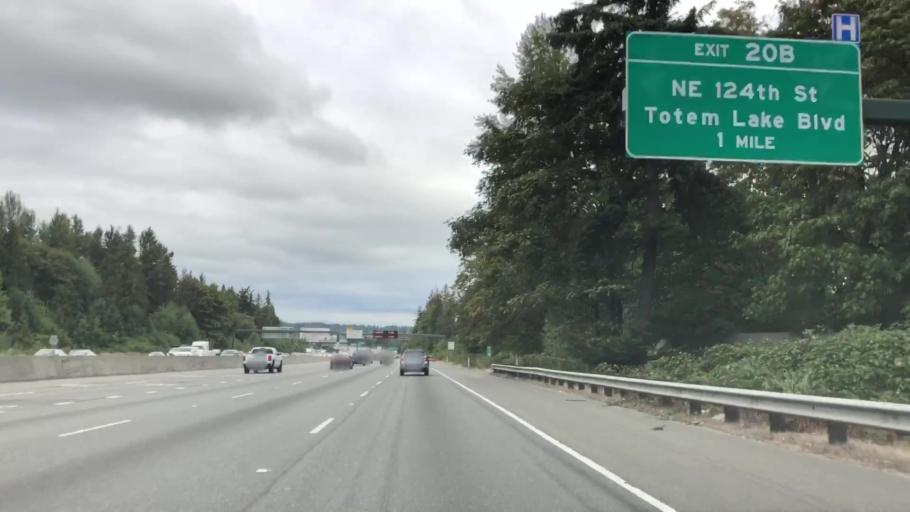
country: US
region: Washington
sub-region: King County
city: Kirkland
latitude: 47.6910
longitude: -122.1810
